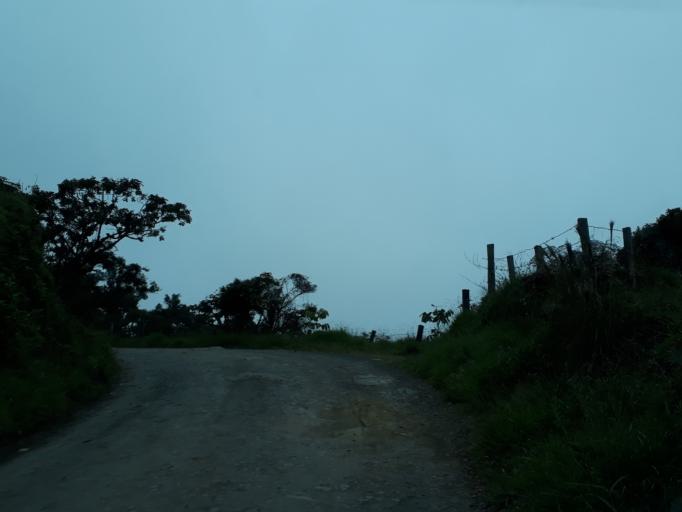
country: CO
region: Boyaca
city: Muzo
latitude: 5.3734
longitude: -74.0742
